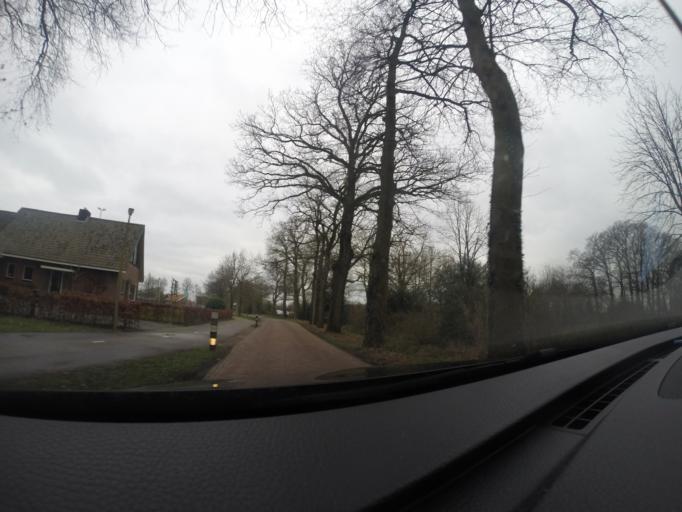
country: NL
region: Overijssel
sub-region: Gemeente Haaksbergen
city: Haaksbergen
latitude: 52.1453
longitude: 6.7274
